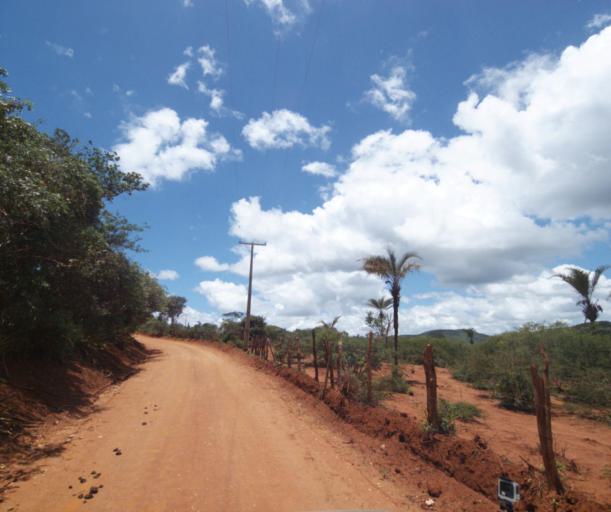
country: BR
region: Bahia
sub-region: Pocoes
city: Pocoes
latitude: -14.3782
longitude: -40.3980
